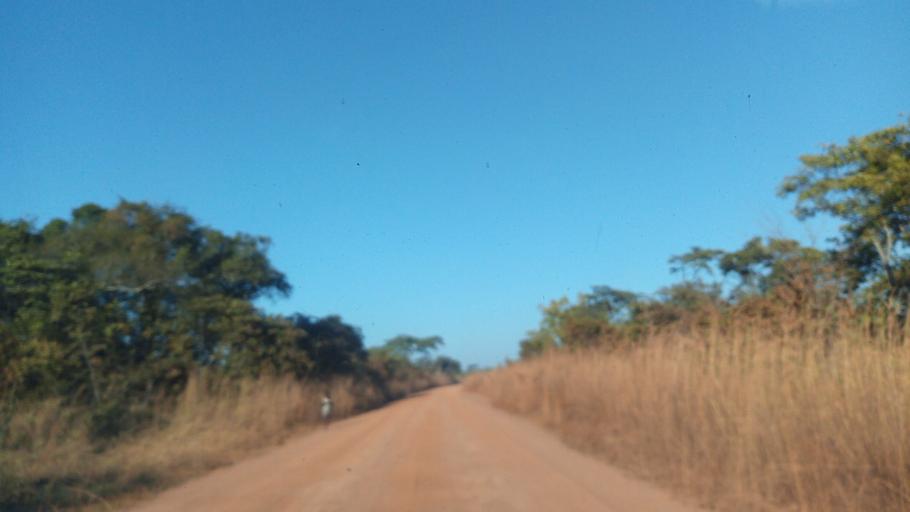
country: ZM
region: Luapula
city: Mwense
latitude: -10.4992
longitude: 28.4818
